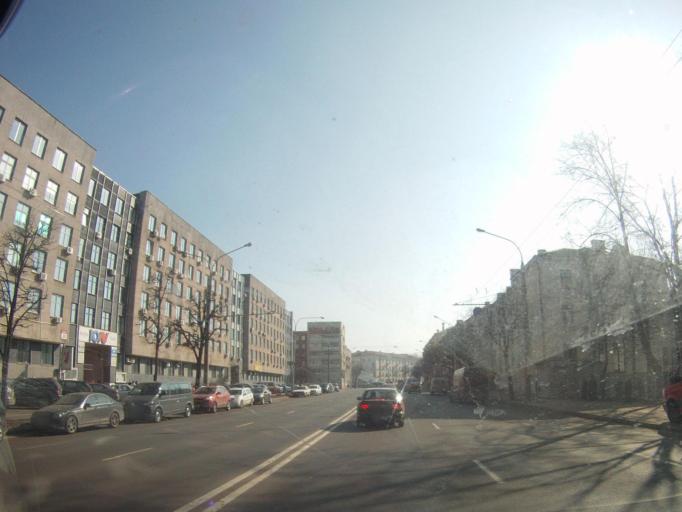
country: BY
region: Minsk
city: Minsk
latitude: 53.9257
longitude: 27.5957
